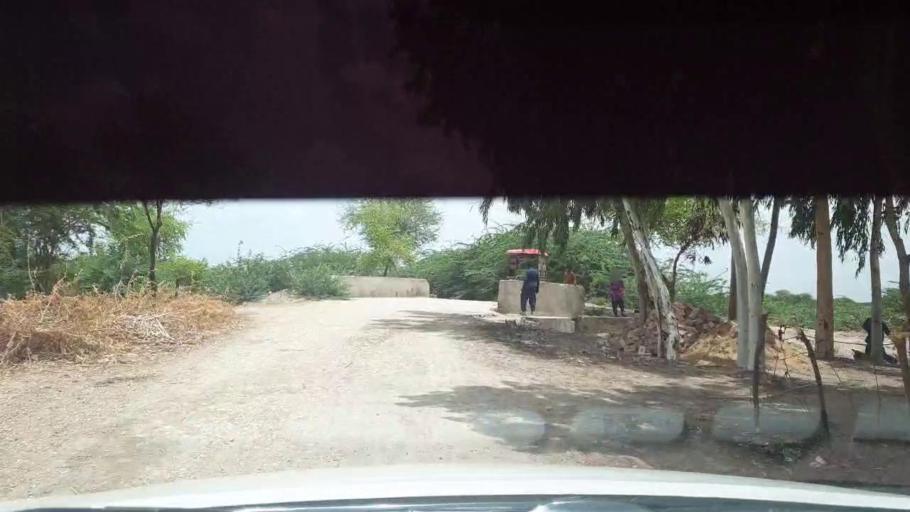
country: PK
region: Sindh
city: Kadhan
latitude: 24.4636
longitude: 69.0350
